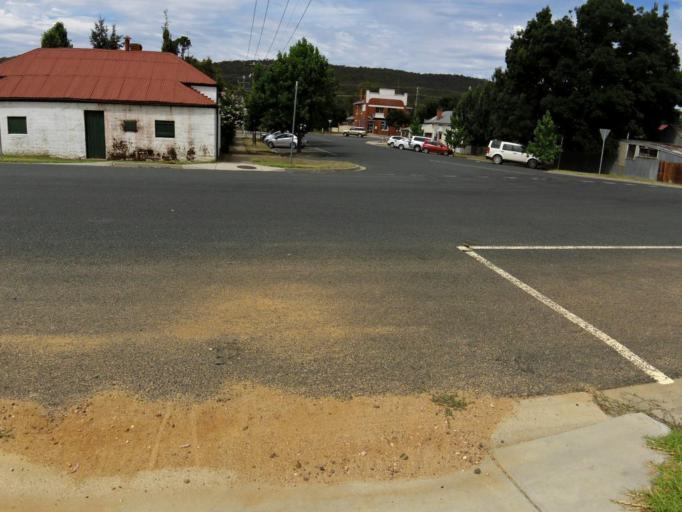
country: AU
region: Victoria
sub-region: Greater Bendigo
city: Kennington
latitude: -36.9246
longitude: 144.7094
